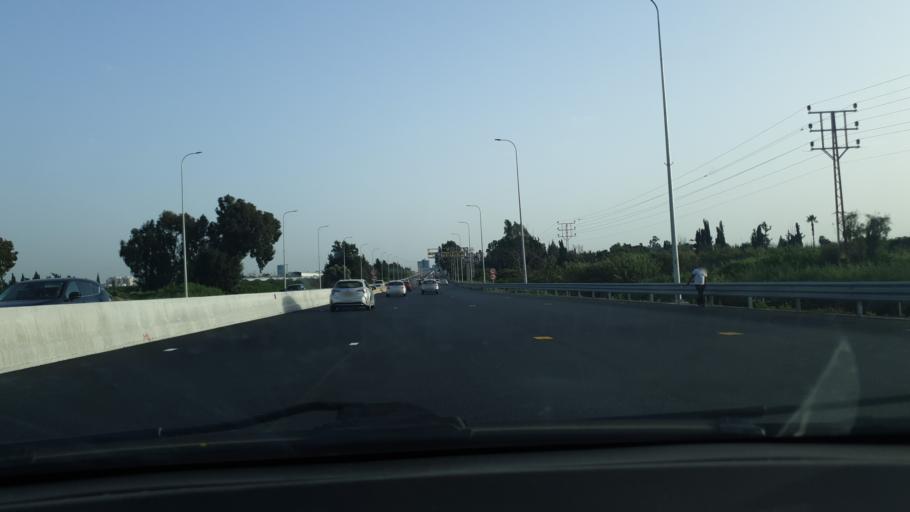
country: IL
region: Central District
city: Ra'anana
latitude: 32.2179
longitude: 34.8833
